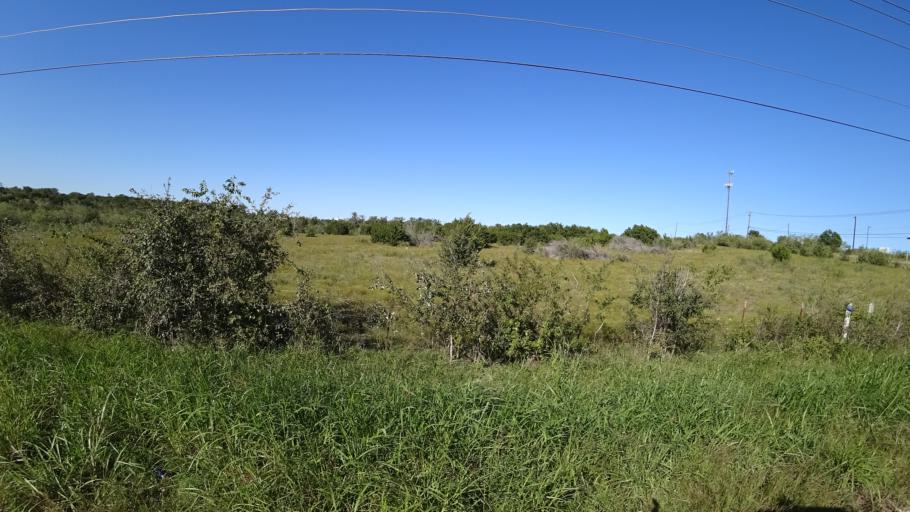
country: US
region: Texas
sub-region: Travis County
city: Hornsby Bend
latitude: 30.2823
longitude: -97.6210
